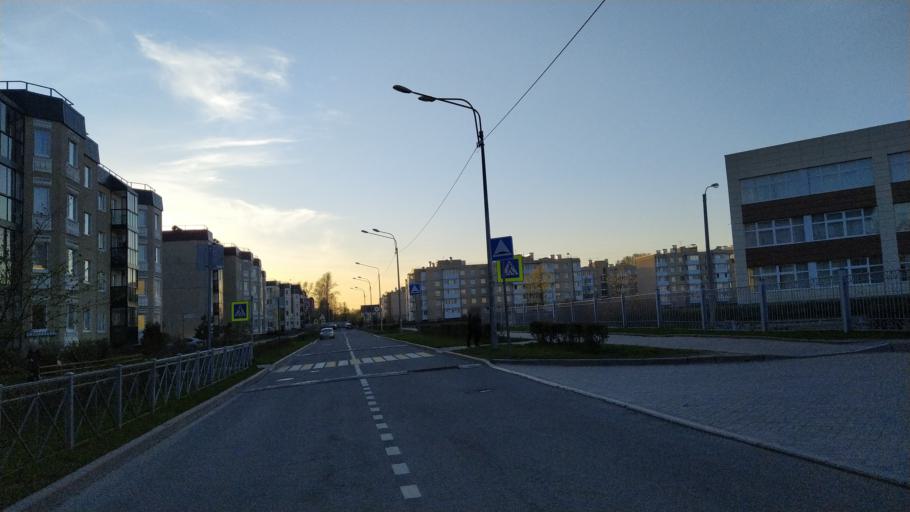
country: RU
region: St.-Petersburg
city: Pushkin
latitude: 59.7040
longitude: 30.3820
